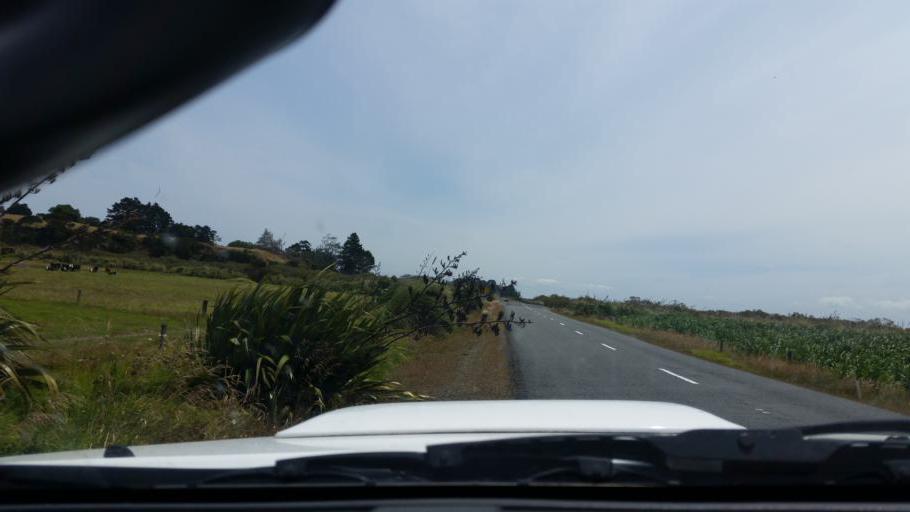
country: NZ
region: Northland
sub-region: Kaipara District
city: Dargaville
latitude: -36.1779
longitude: 174.0289
